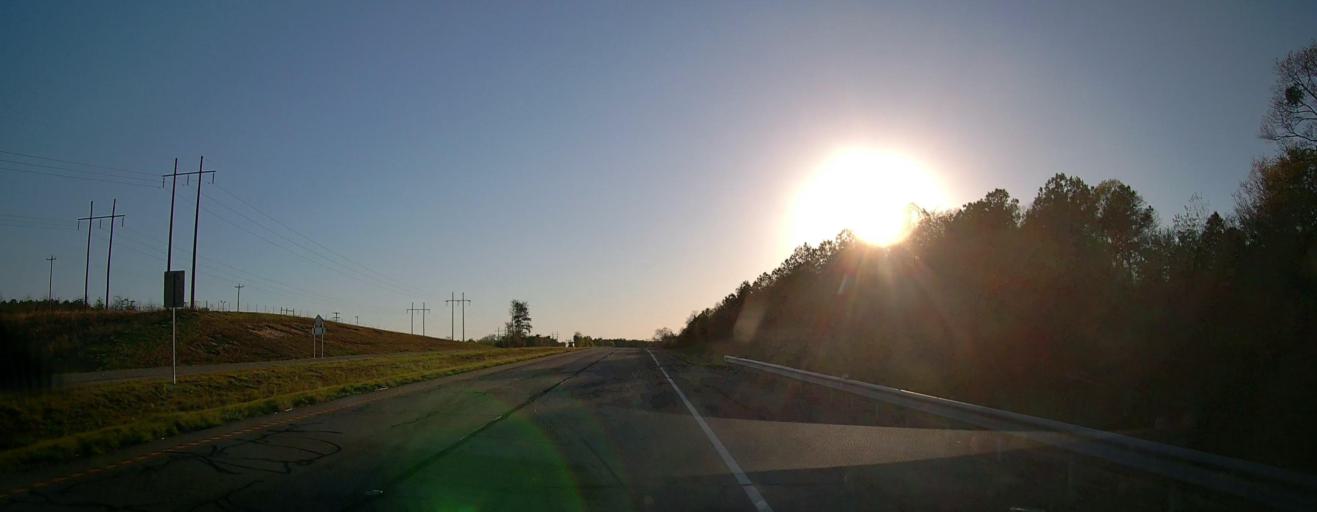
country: US
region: Georgia
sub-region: Wilkinson County
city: Gordon
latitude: 32.8986
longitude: -83.3042
